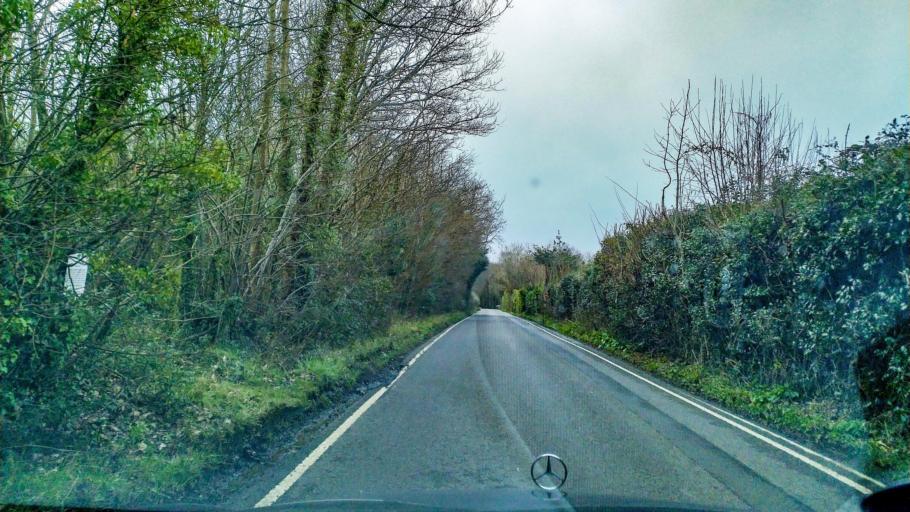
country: GB
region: England
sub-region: Surrey
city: Dorking
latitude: 51.2116
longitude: -0.3233
